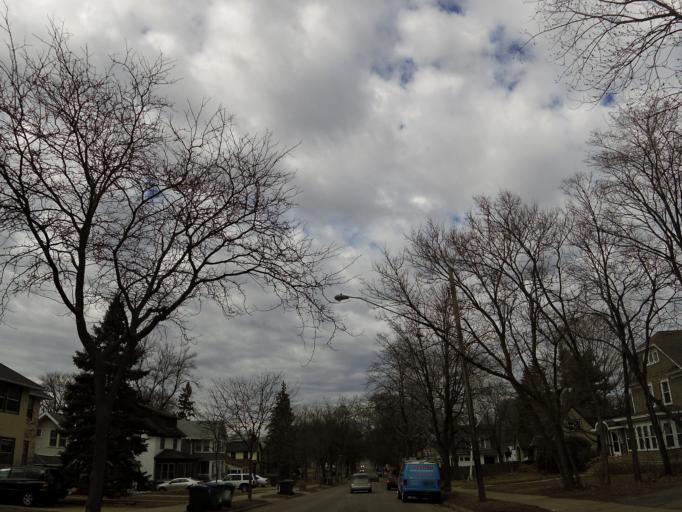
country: US
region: Minnesota
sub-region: Hennepin County
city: Saint Louis Park
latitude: 44.9239
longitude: -93.3189
